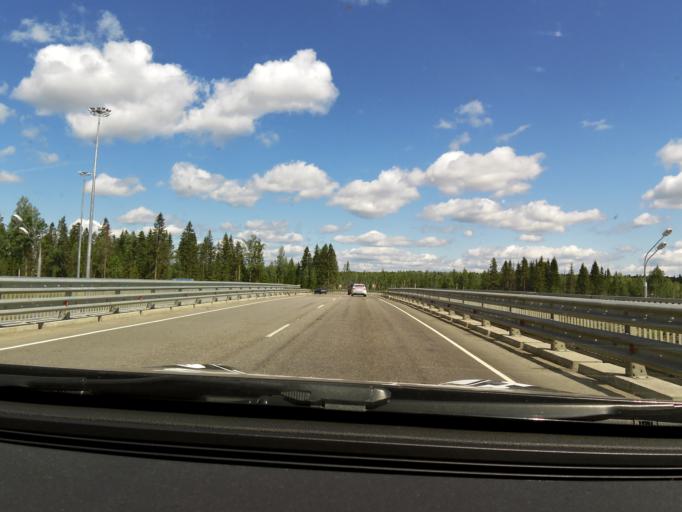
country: RU
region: Tverskaya
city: Bologoye
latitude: 57.7081
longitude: 34.1933
